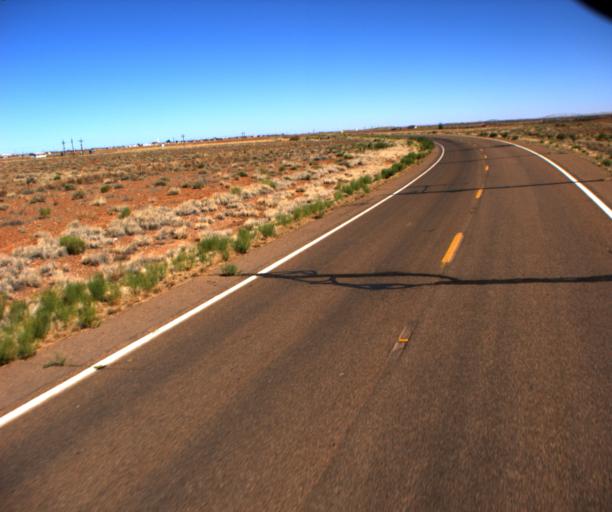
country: US
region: Arizona
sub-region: Coconino County
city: LeChee
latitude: 35.2880
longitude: -110.9845
